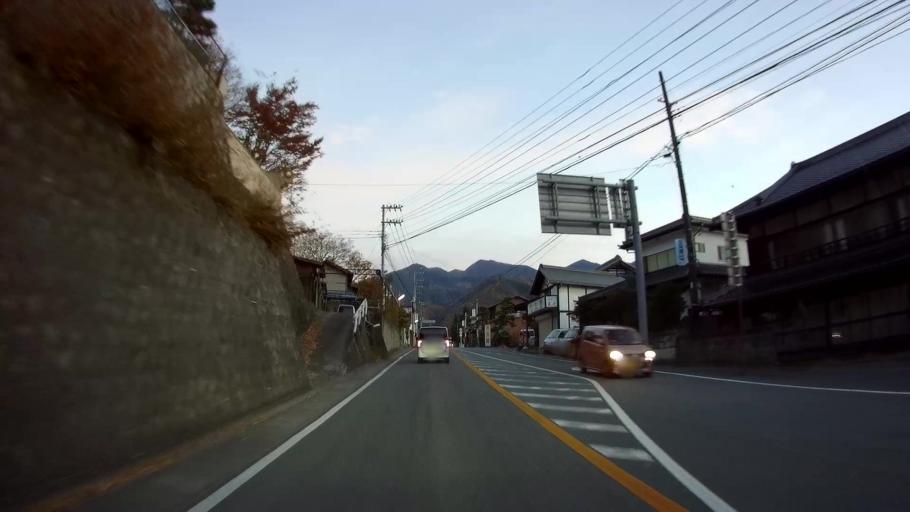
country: JP
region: Yamanashi
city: Enzan
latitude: 35.6600
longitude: 138.7339
